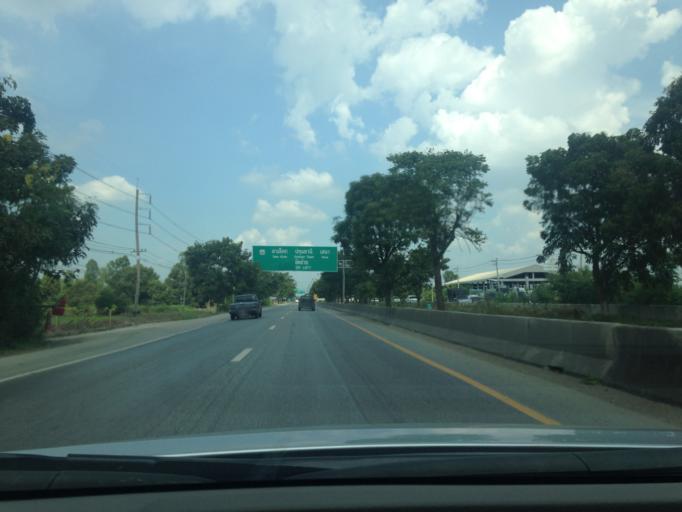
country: TH
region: Pathum Thani
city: Sam Khok
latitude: 14.0860
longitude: 100.5096
